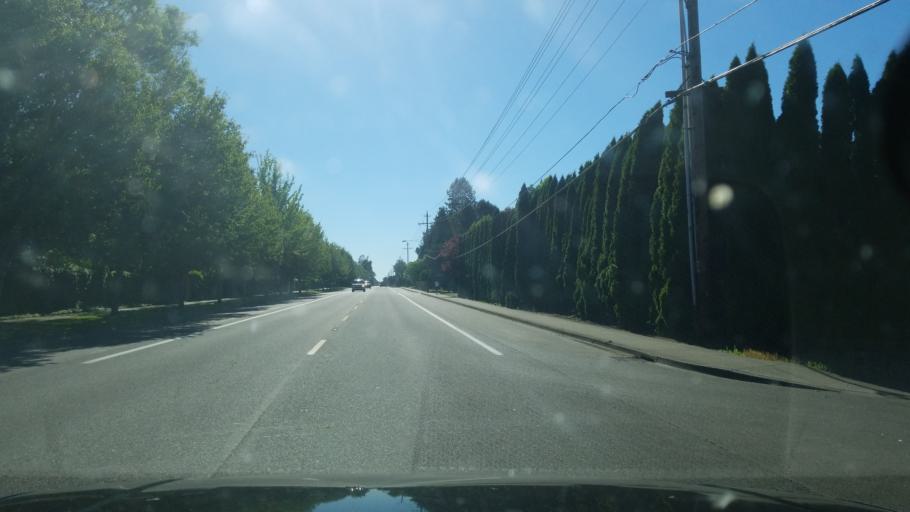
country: US
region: Oregon
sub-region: Yamhill County
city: McMinnville
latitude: 45.2263
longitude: -123.2168
